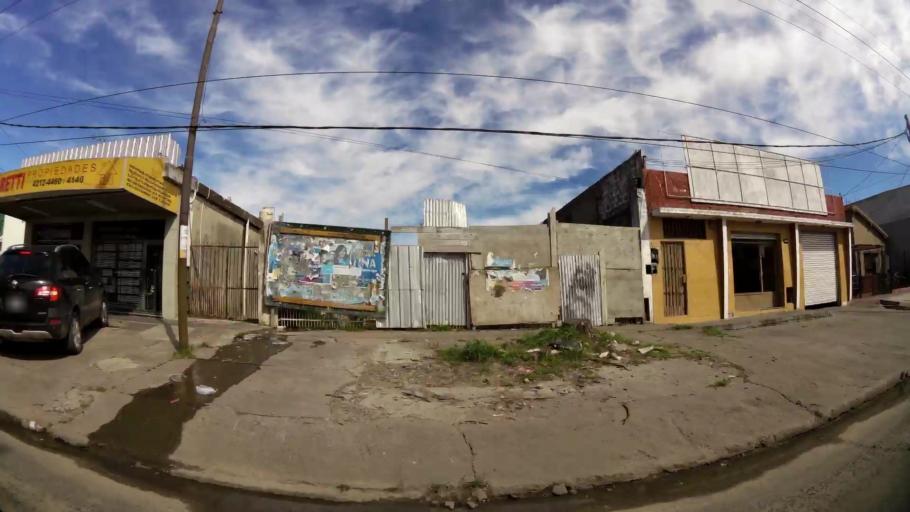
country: AR
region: Buenos Aires
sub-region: Partido de Quilmes
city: Quilmes
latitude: -34.7746
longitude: -58.3028
